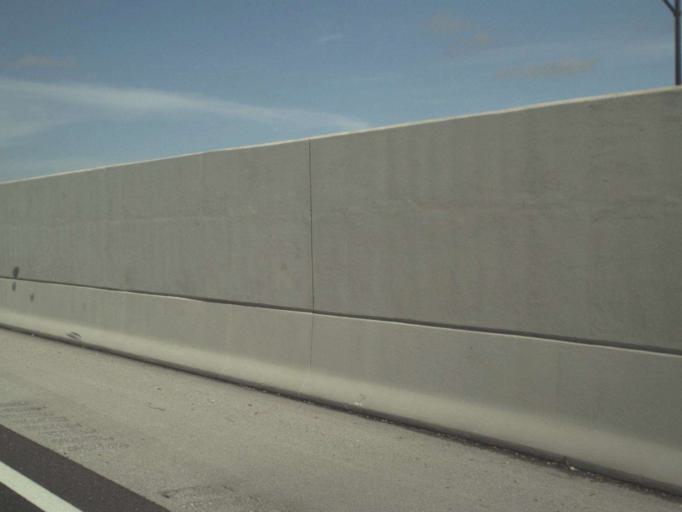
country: US
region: Florida
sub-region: Broward County
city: Pine Island Ridge
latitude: 26.1075
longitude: -80.2831
